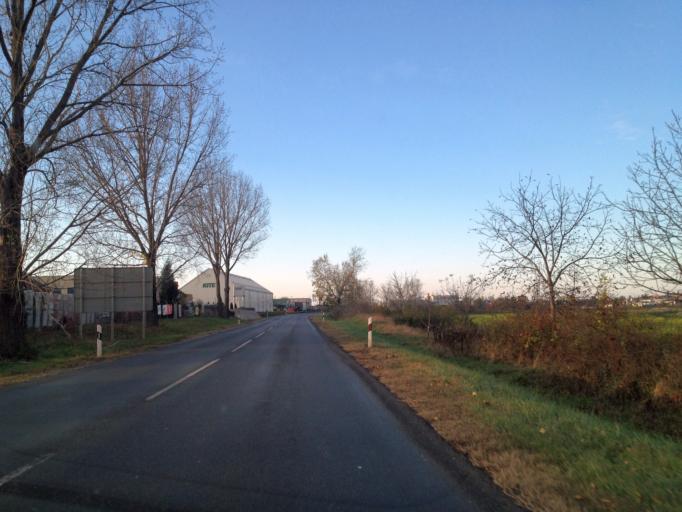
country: HU
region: Gyor-Moson-Sopron
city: Gyorujbarat
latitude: 47.6454
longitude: 17.6606
